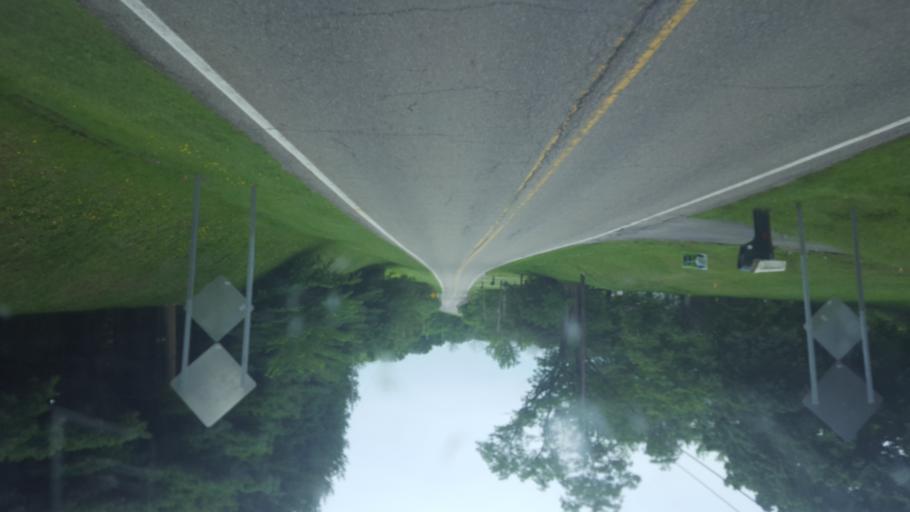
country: US
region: Ohio
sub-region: Trumbull County
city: Morgandale
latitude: 41.2990
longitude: -80.7555
